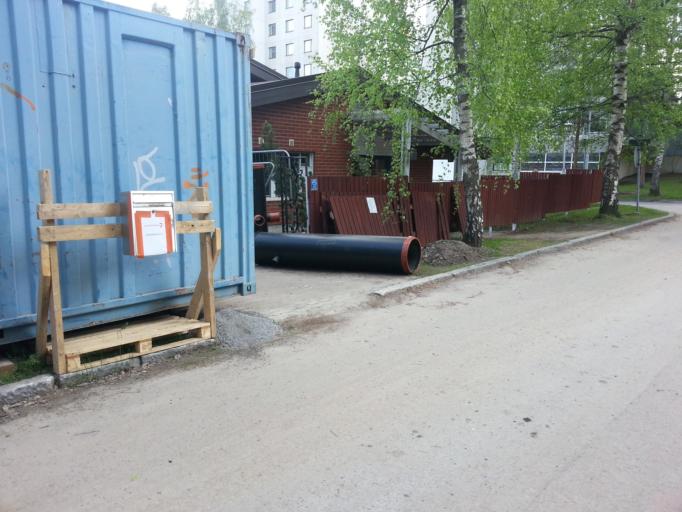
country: FI
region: Pirkanmaa
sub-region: Tampere
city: Tampere
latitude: 61.4561
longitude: 23.8435
